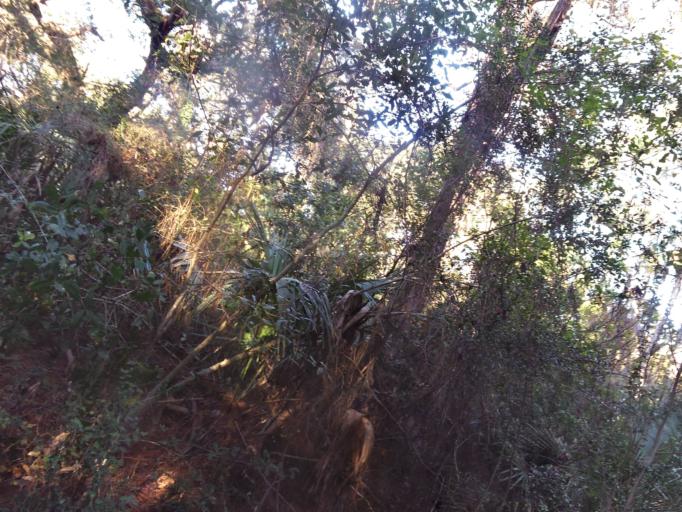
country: US
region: Florida
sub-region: Duval County
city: Atlantic Beach
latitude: 30.4777
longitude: -81.4174
